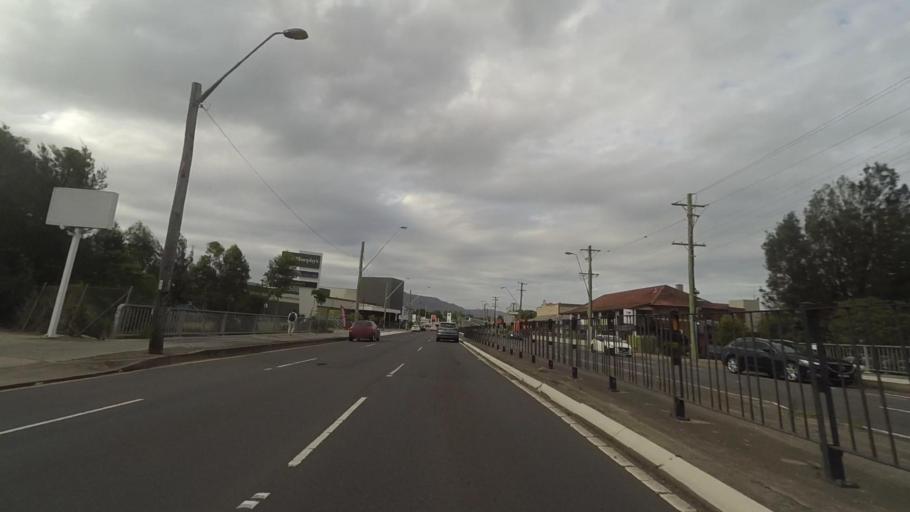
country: AU
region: New South Wales
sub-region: Wollongong
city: Gwynneville
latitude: -34.4137
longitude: 150.8928
